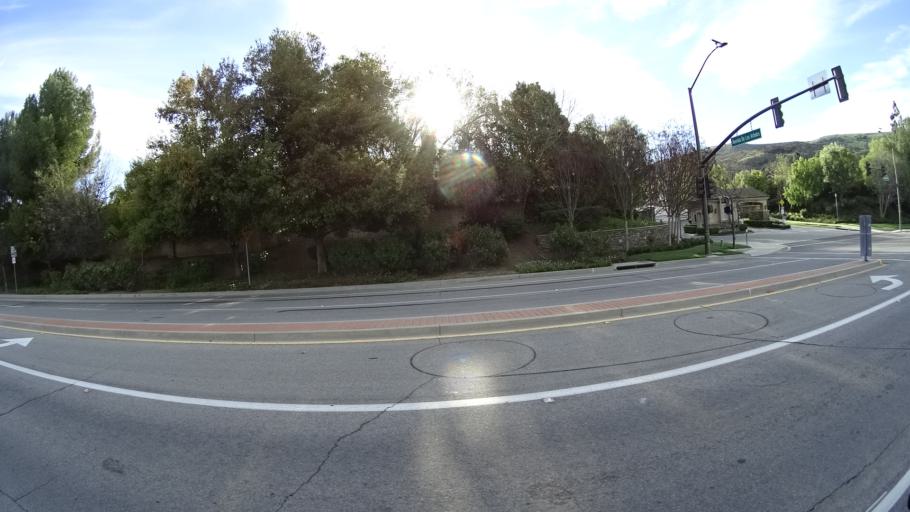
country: US
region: California
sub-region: Ventura County
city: Thousand Oaks
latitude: 34.2147
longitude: -118.8232
